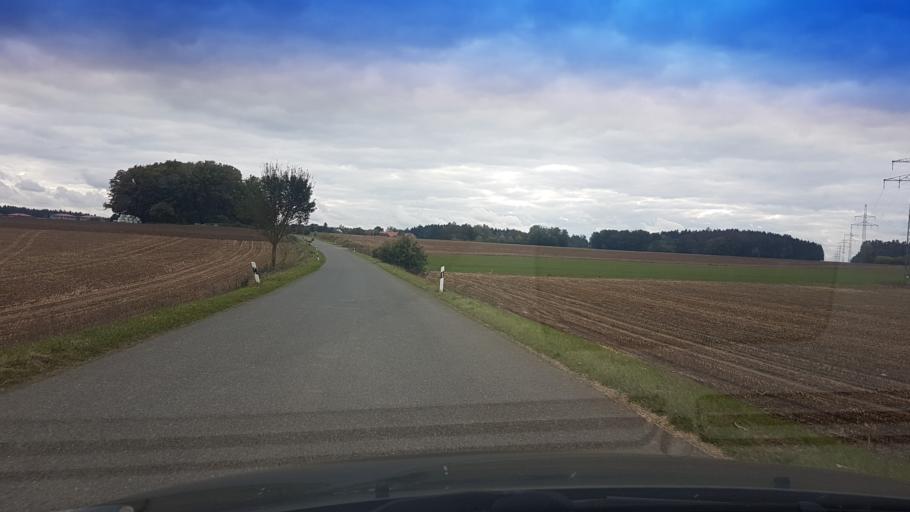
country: DE
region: Bavaria
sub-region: Upper Franconia
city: Wonsees
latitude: 50.0181
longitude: 11.2618
